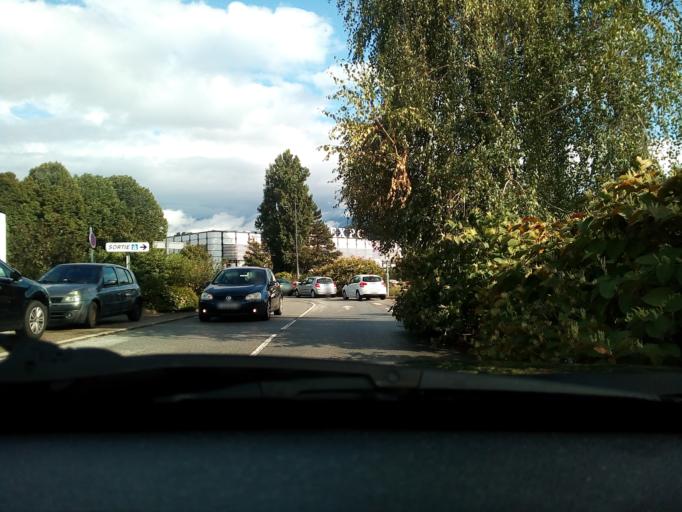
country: FR
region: Rhone-Alpes
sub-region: Departement de l'Isere
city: Echirolles
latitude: 45.1562
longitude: 5.7329
